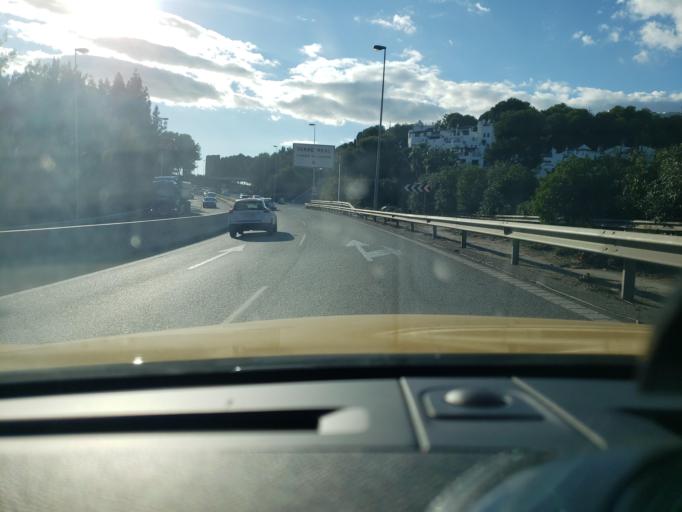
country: ES
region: Andalusia
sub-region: Provincia de Malaga
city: Marbella
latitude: 36.5070
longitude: -4.8428
